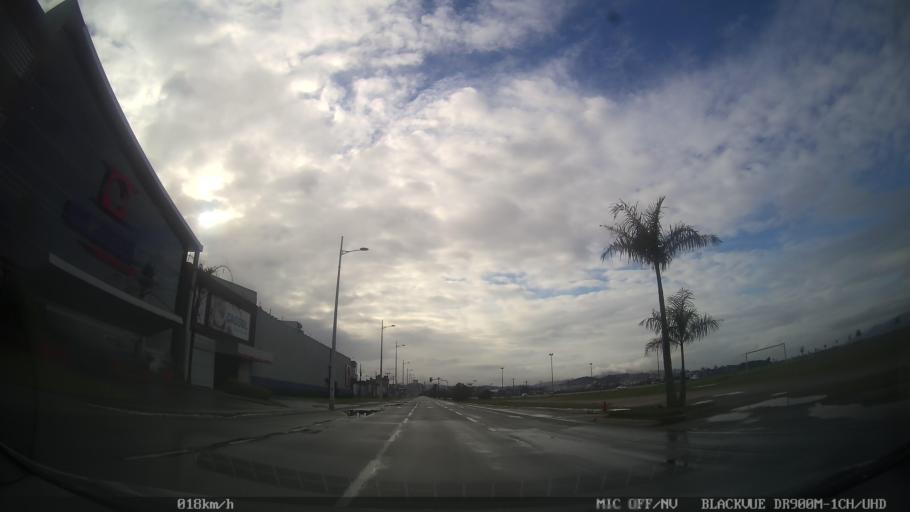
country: BR
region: Santa Catarina
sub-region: Sao Jose
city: Campinas
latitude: -27.6027
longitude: -48.6160
